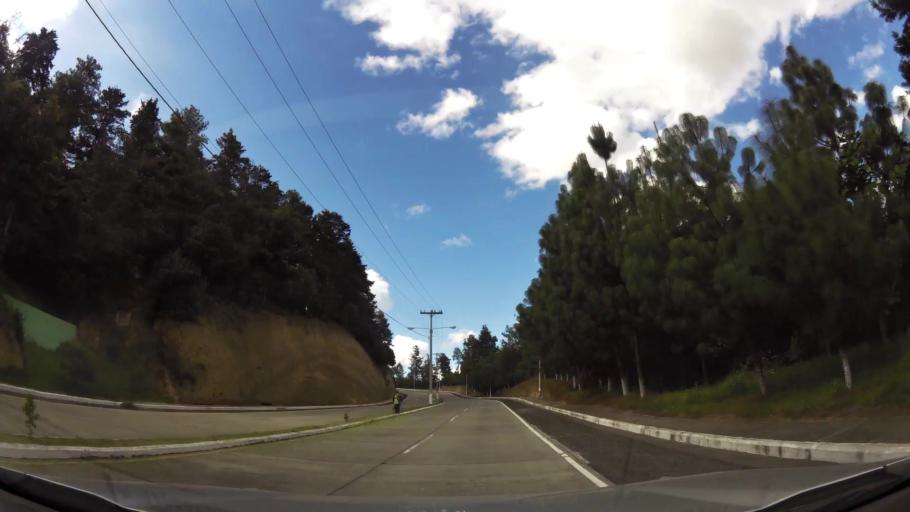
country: GT
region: Quetzaltenango
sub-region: Municipio de La Esperanza
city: La Esperanza
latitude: 14.8366
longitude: -91.5541
